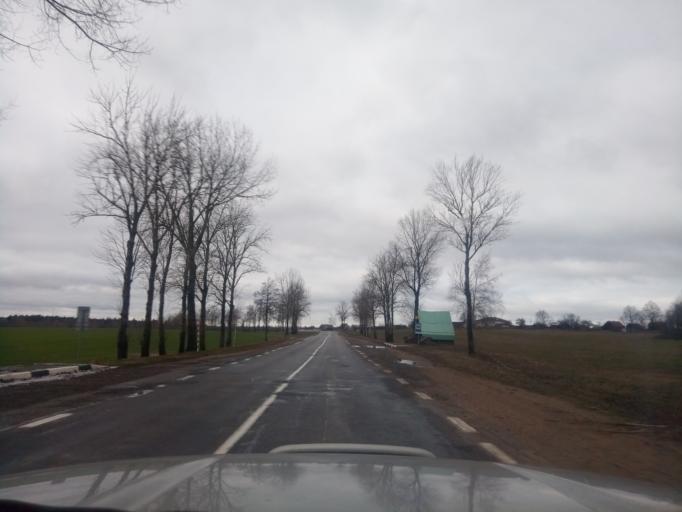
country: BY
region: Minsk
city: Kapyl'
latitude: 53.1702
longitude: 27.1334
